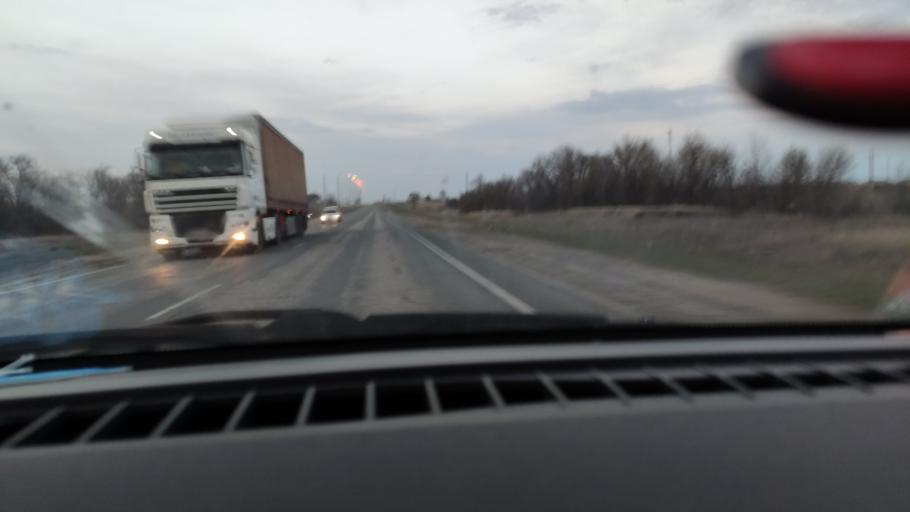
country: RU
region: Saratov
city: Sinodskoye
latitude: 51.9822
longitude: 46.6592
